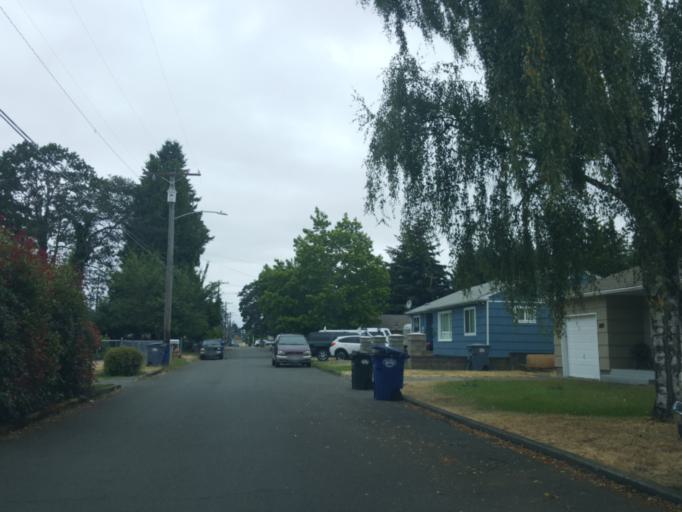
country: US
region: Washington
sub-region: Pierce County
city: Lakewood
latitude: 47.1701
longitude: -122.5129
